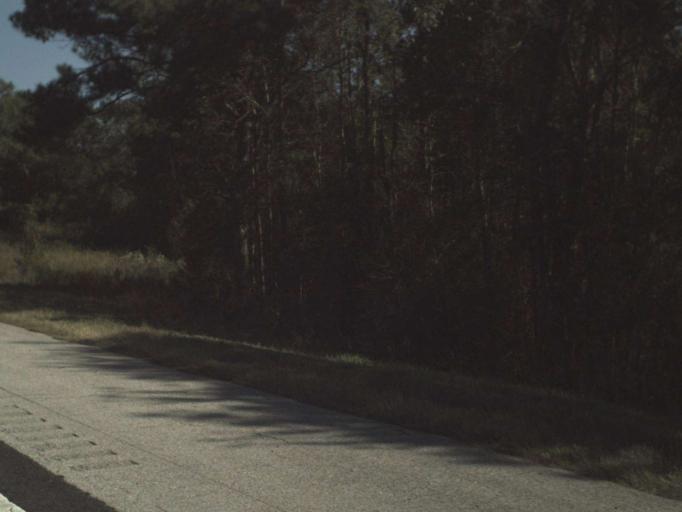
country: US
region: Florida
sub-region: Holmes County
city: Bonifay
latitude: 30.7605
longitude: -85.7877
